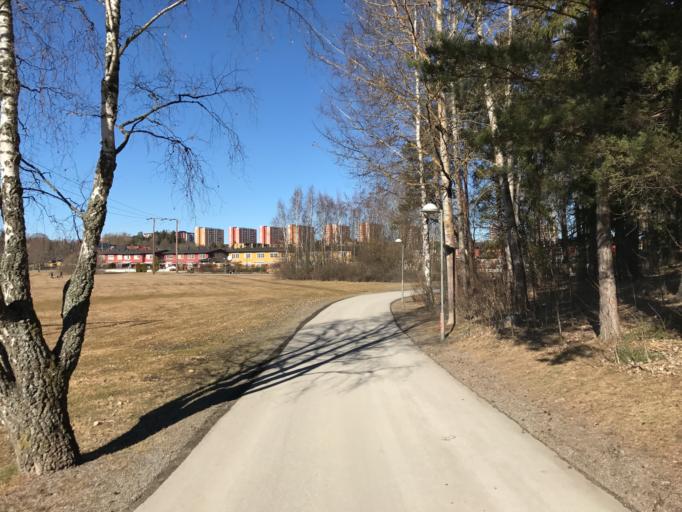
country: SE
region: Stockholm
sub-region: Stockholms Kommun
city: Kista
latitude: 59.4082
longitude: 17.9167
